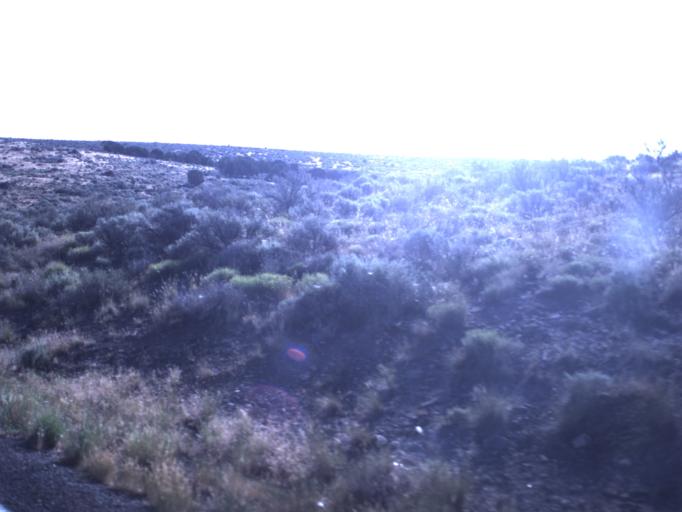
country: US
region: Utah
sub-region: Iron County
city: Parowan
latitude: 38.0749
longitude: -112.9586
